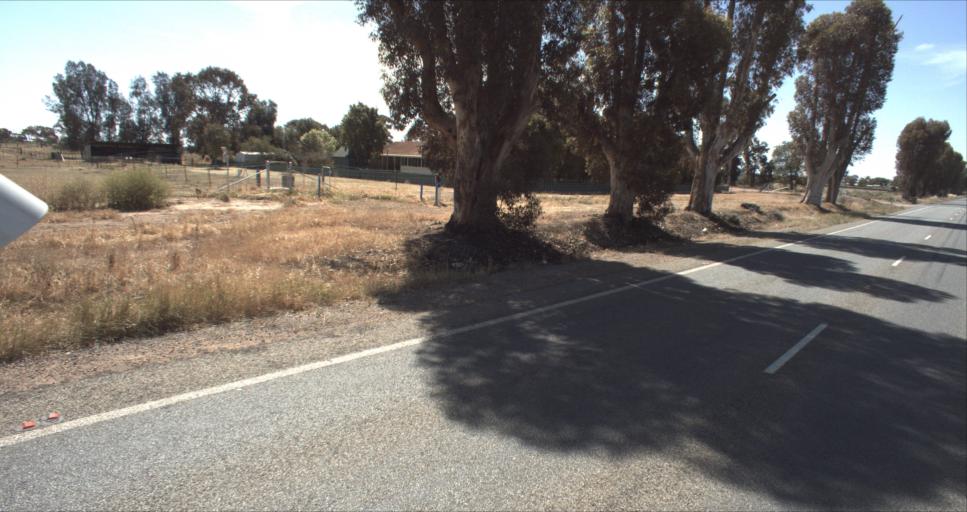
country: AU
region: New South Wales
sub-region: Leeton
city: Leeton
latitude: -34.5907
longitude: 146.4138
